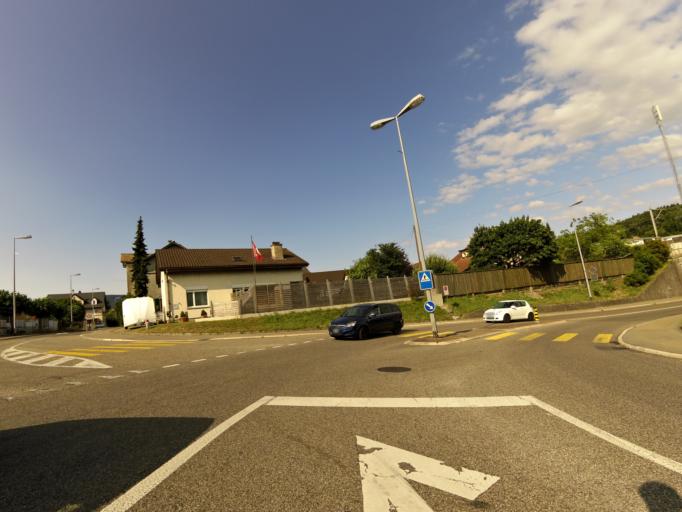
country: CH
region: Solothurn
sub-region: Bezirk Olten
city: Schonenwerd
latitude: 47.3744
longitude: 8.0008
